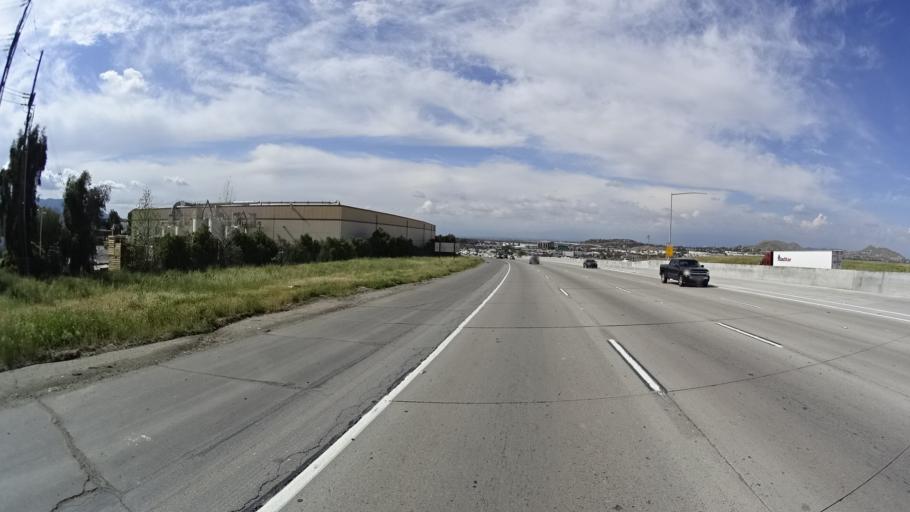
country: US
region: California
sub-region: Riverside County
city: Home Gardens
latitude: 33.8606
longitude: -117.5374
